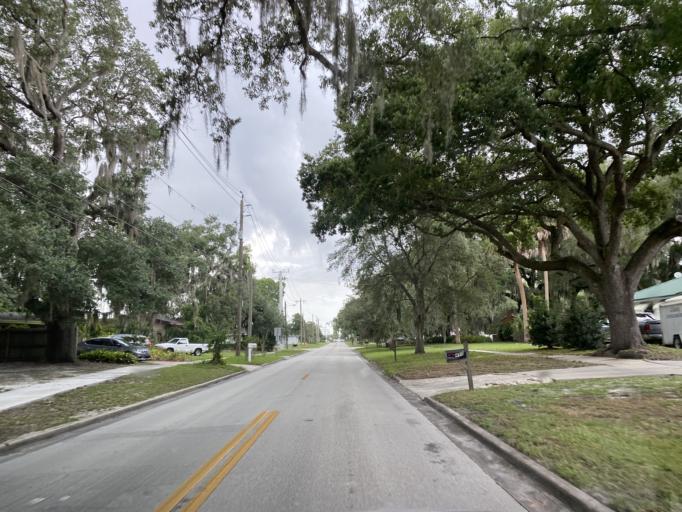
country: US
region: Florida
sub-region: Seminole County
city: Sanford
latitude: 28.8075
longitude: -81.2551
